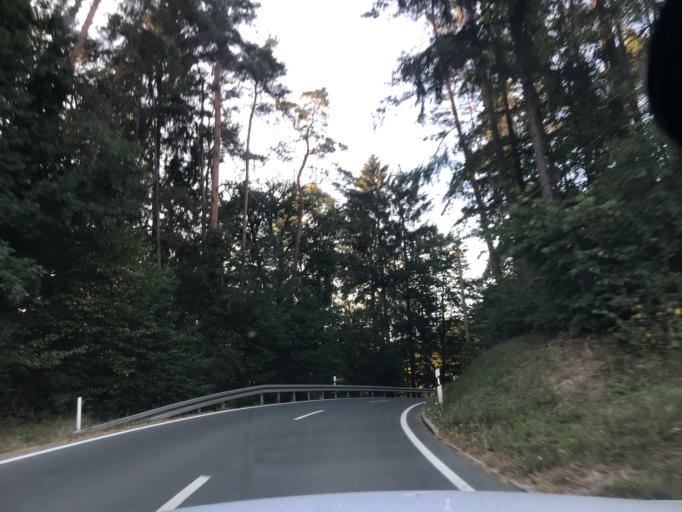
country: DE
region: Bavaria
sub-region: Upper Franconia
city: Pegnitz
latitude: 49.7294
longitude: 11.5574
